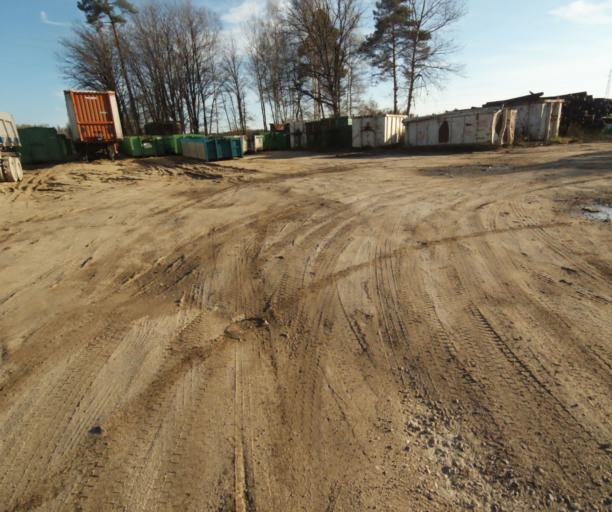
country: FR
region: Limousin
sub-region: Departement de la Correze
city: Correze
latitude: 45.3337
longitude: 1.8822
